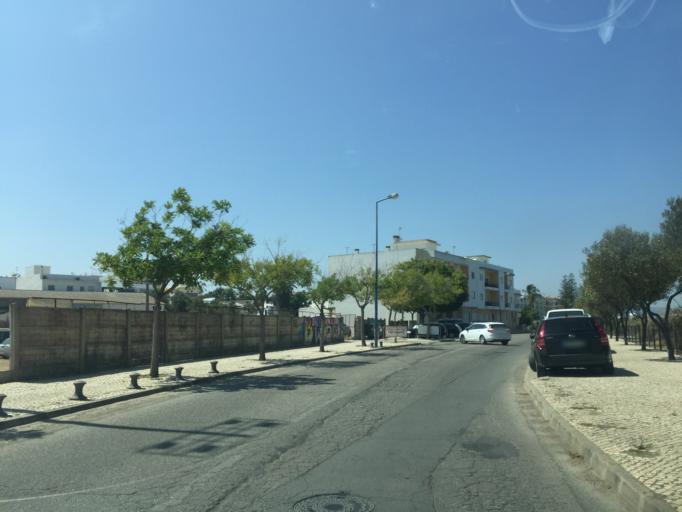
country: PT
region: Faro
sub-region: Olhao
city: Laranjeiro
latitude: 37.0569
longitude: -7.7463
